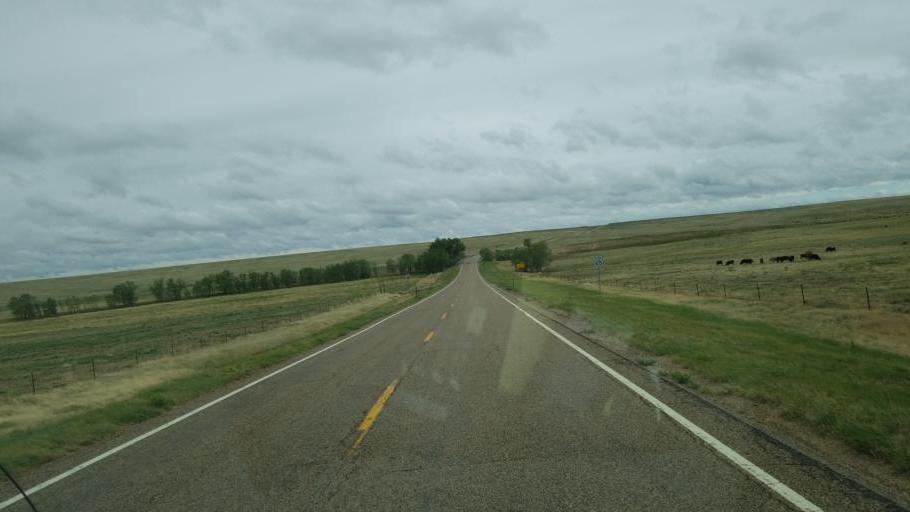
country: US
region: Colorado
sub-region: Lincoln County
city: Hugo
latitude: 38.8500
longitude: -103.4806
